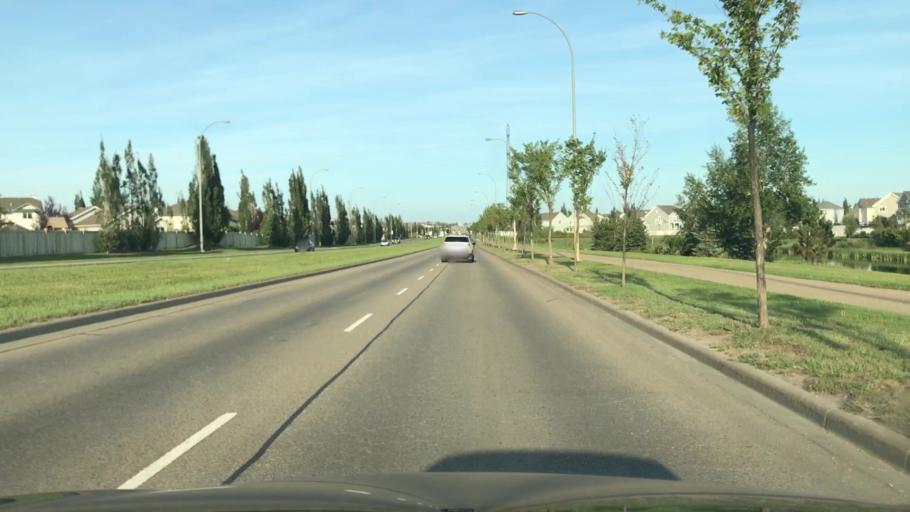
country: CA
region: Alberta
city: Beaumont
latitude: 53.4248
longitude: -113.4714
